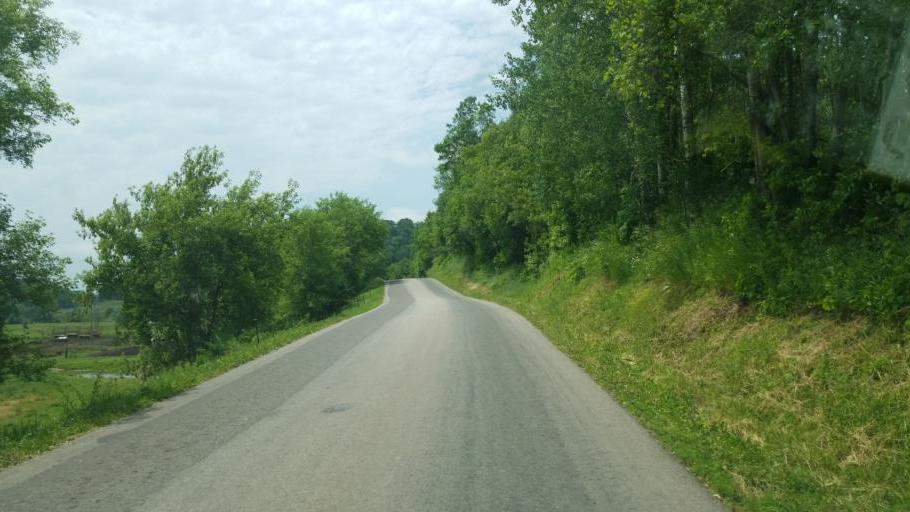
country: US
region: Wisconsin
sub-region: Monroe County
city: Cashton
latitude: 43.7258
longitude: -90.6658
